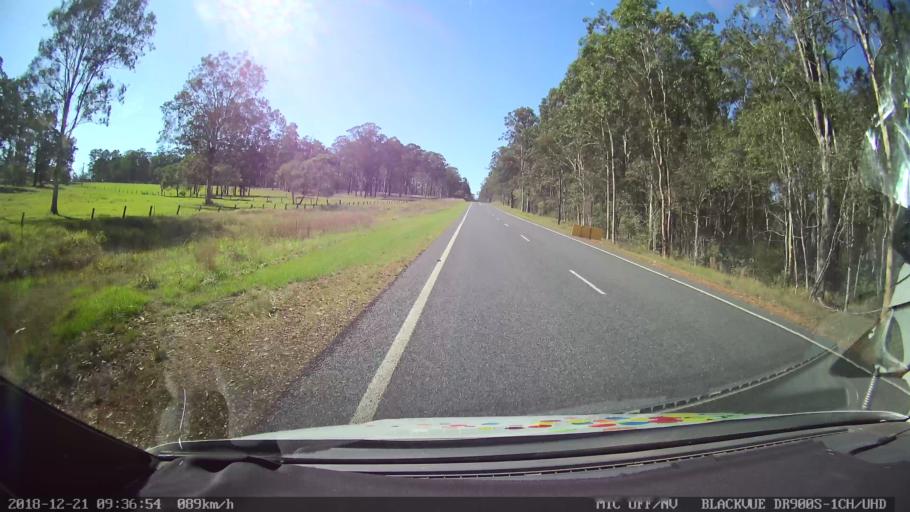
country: AU
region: New South Wales
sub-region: Clarence Valley
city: Grafton
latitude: -29.5296
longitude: 152.9848
